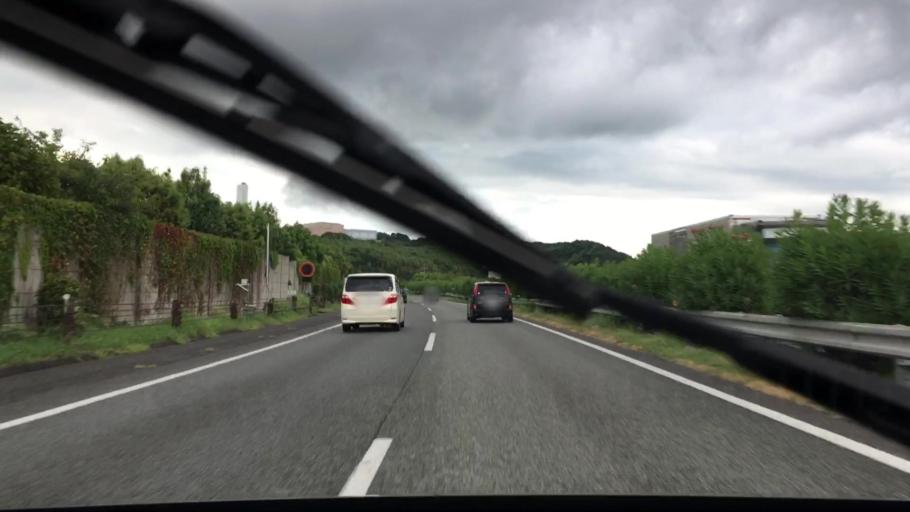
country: JP
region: Fukuoka
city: Sasaguri
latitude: 33.6357
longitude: 130.4907
